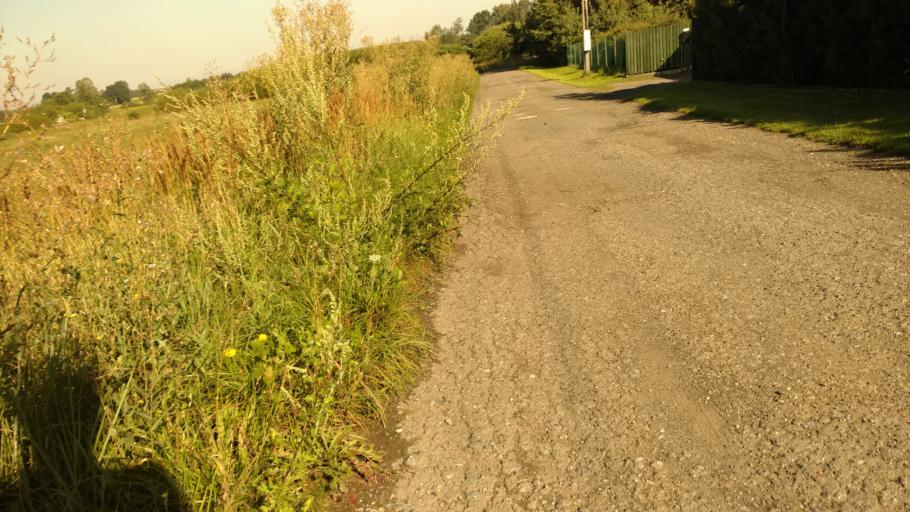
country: PL
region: Silesian Voivodeship
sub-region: Powiat pszczynski
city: Jankowice
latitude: 49.9846
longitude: 18.9907
